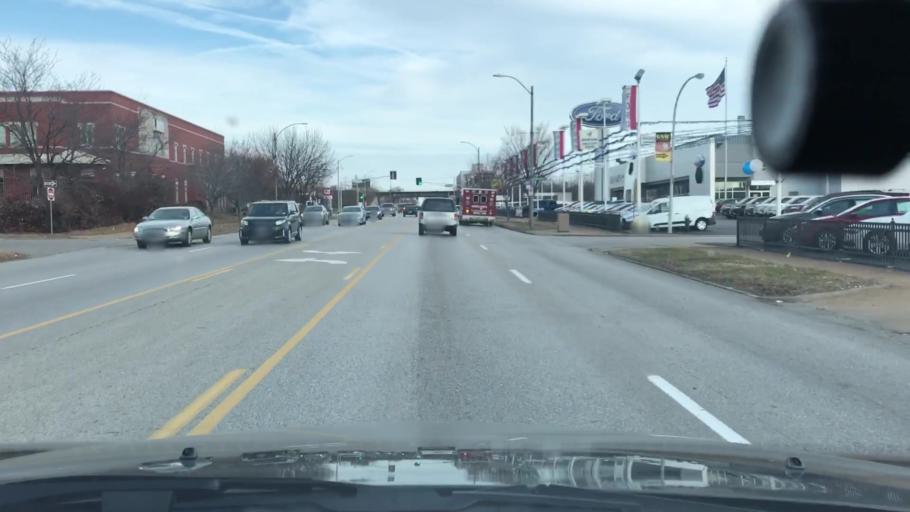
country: US
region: Missouri
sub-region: Saint Louis County
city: Maplewood
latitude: 38.5983
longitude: -90.2705
